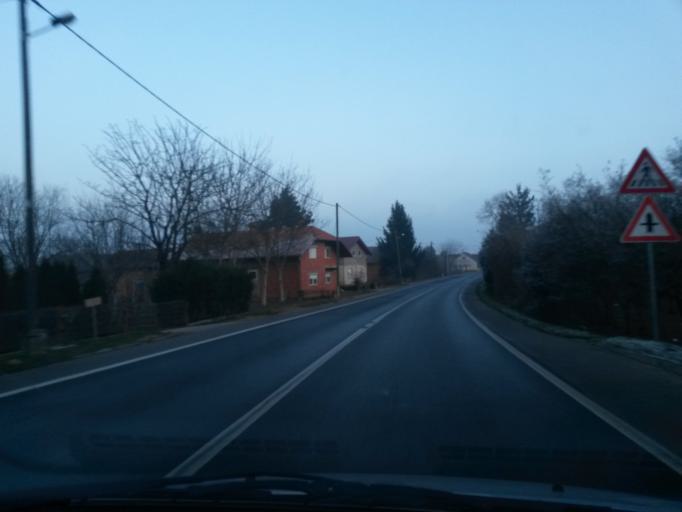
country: HR
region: Varazdinska
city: Ludbreg
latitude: 46.2210
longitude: 16.6784
